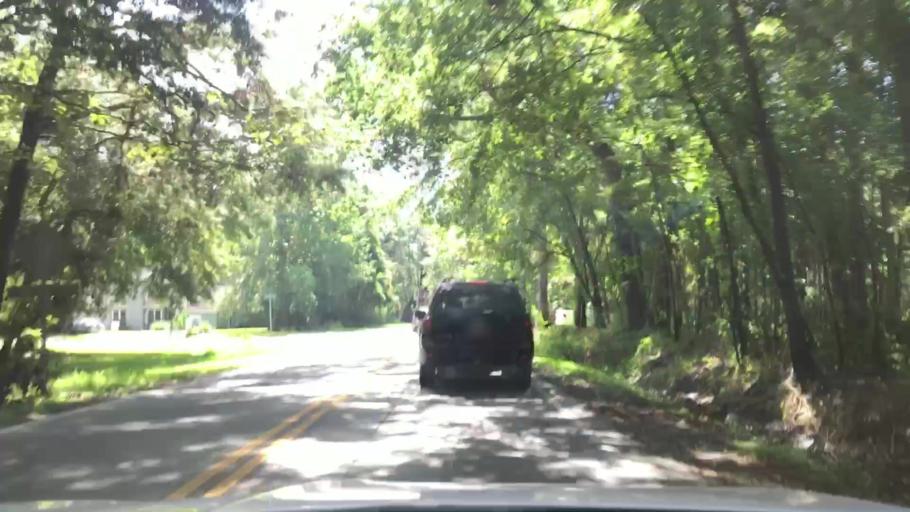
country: US
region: South Carolina
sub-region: Charleston County
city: Shell Point
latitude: 32.8392
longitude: -80.0523
